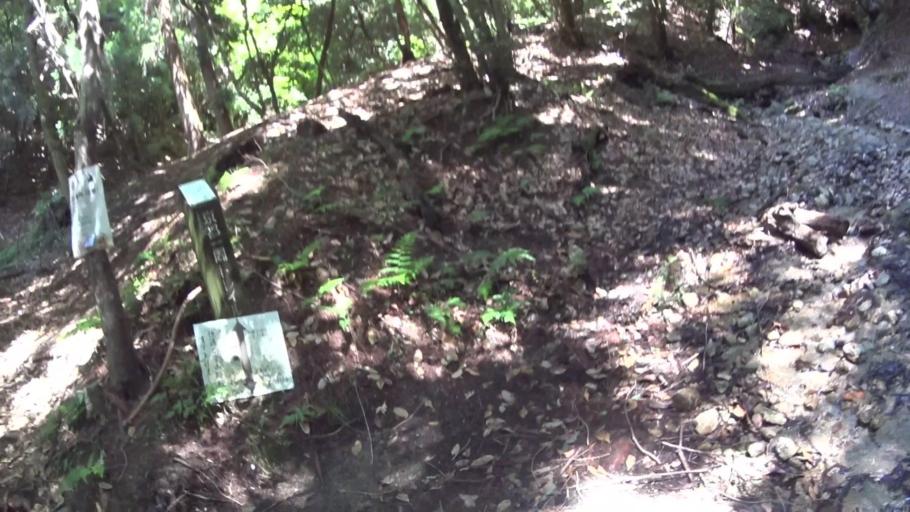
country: JP
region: Kyoto
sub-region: Kyoto-shi
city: Kamigyo-ku
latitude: 35.0379
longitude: 135.7955
